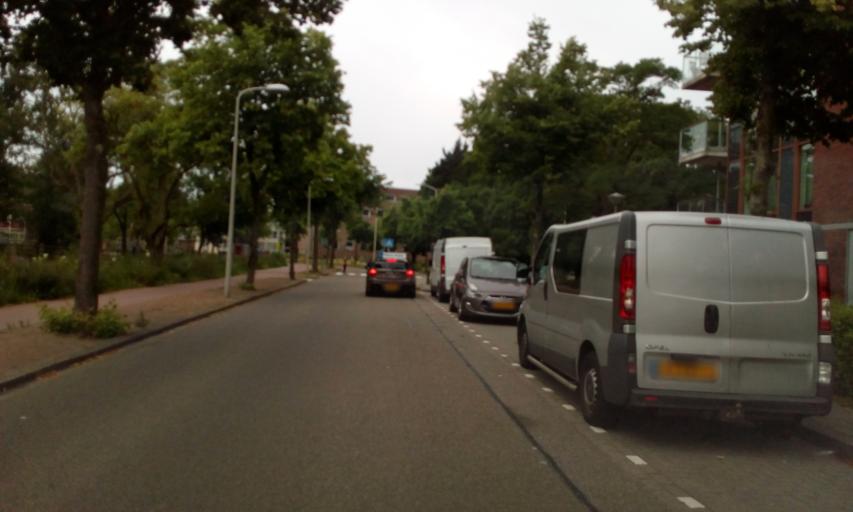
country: NL
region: South Holland
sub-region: Gemeente Rijswijk
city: Rijswijk
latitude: 52.0461
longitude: 4.2992
